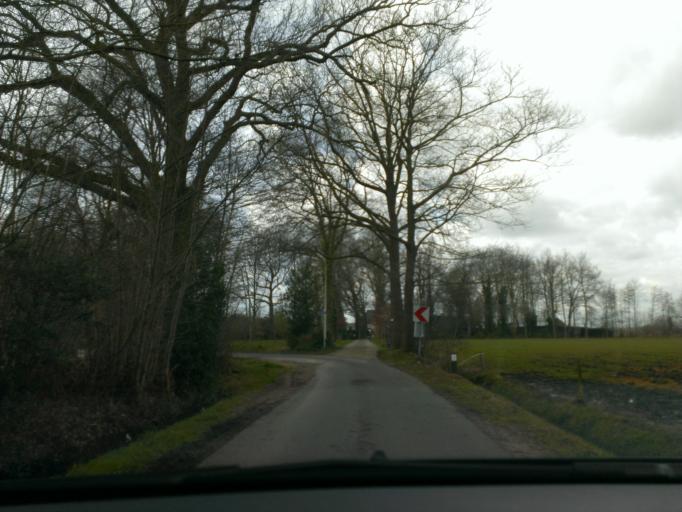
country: NL
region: Overijssel
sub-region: Gemeente Borne
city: Borne
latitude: 52.3072
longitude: 6.7325
